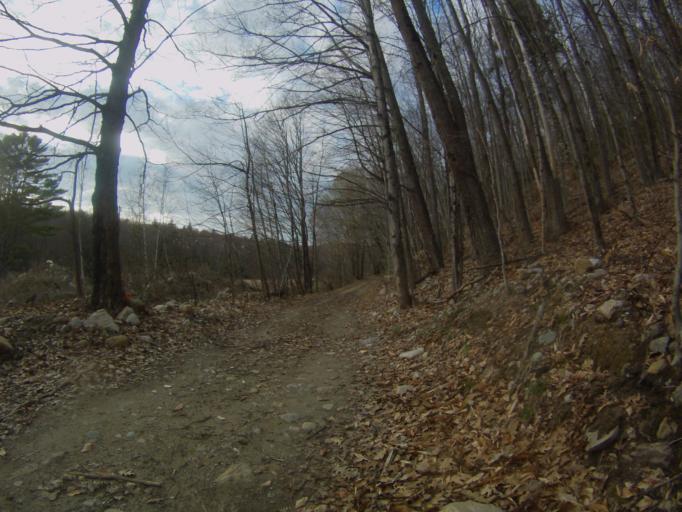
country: US
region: Vermont
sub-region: Rutland County
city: Brandon
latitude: 43.8389
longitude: -73.0407
